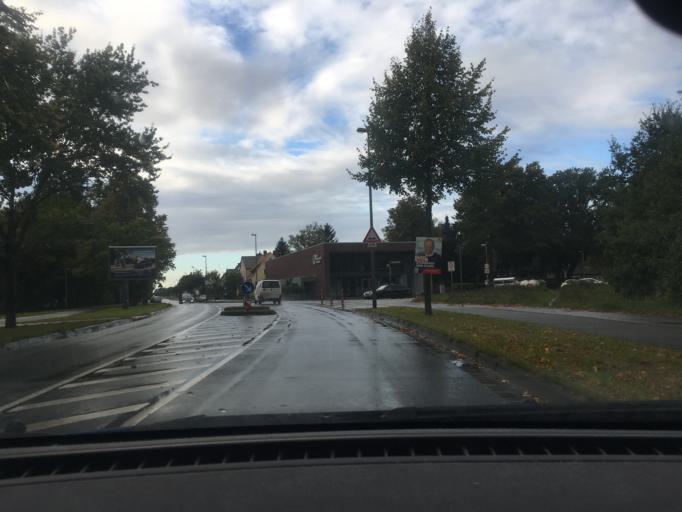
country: DE
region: Lower Saxony
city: Langenhagen
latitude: 52.4202
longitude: 9.7916
